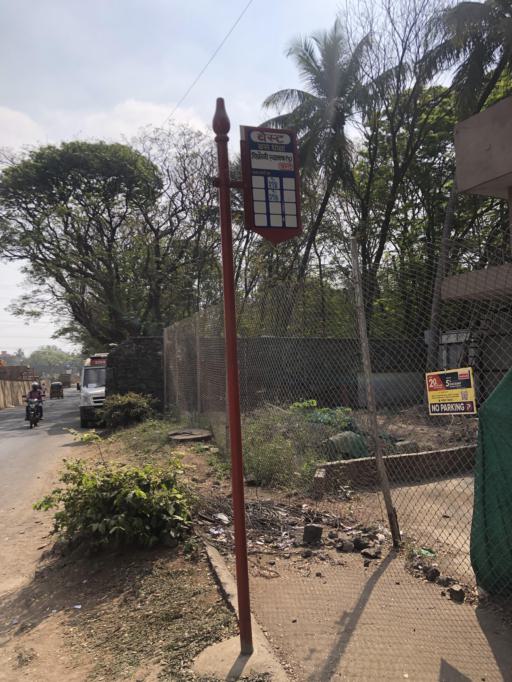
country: IN
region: Maharashtra
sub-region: Mumbai Suburban
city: Powai
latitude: 19.1103
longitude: 72.9290
